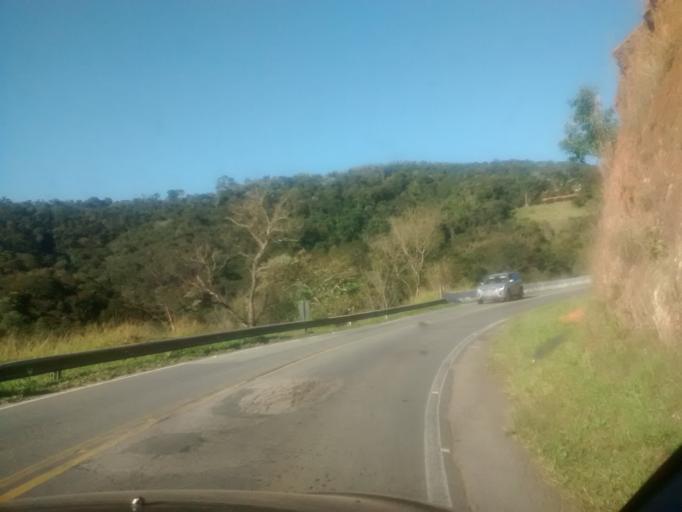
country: BR
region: Sao Paulo
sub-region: Campos Do Jordao
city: Campos do Jordao
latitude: -22.8281
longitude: -45.7109
